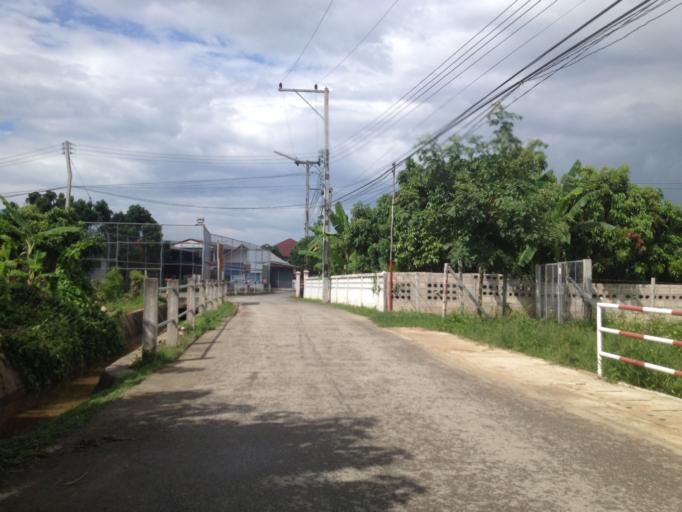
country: TH
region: Chiang Mai
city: Hang Dong
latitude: 18.6950
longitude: 98.9105
